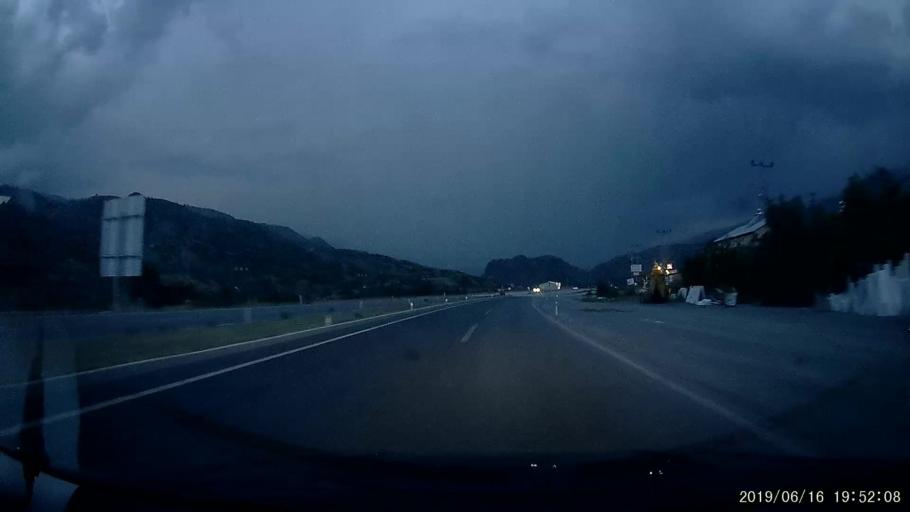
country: TR
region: Sivas
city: Koyulhisar
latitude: 40.2852
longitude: 37.8087
